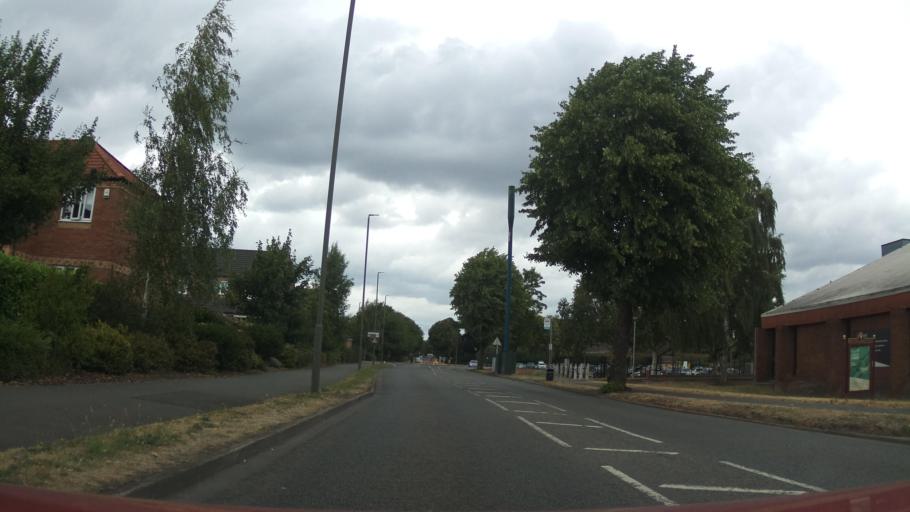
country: GB
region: England
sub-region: Derbyshire
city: Long Eaton
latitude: 52.8937
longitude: -1.2909
